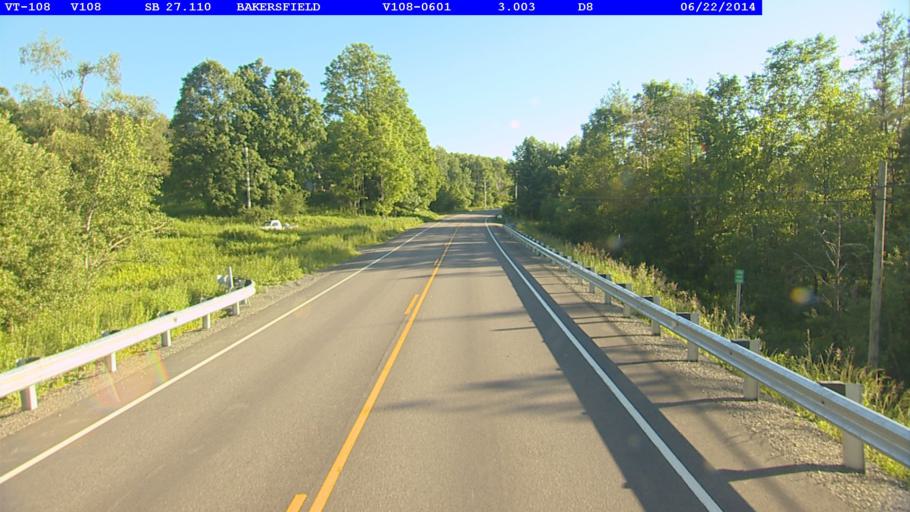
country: US
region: Vermont
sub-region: Franklin County
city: Enosburg Falls
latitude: 44.7733
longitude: -72.8073
